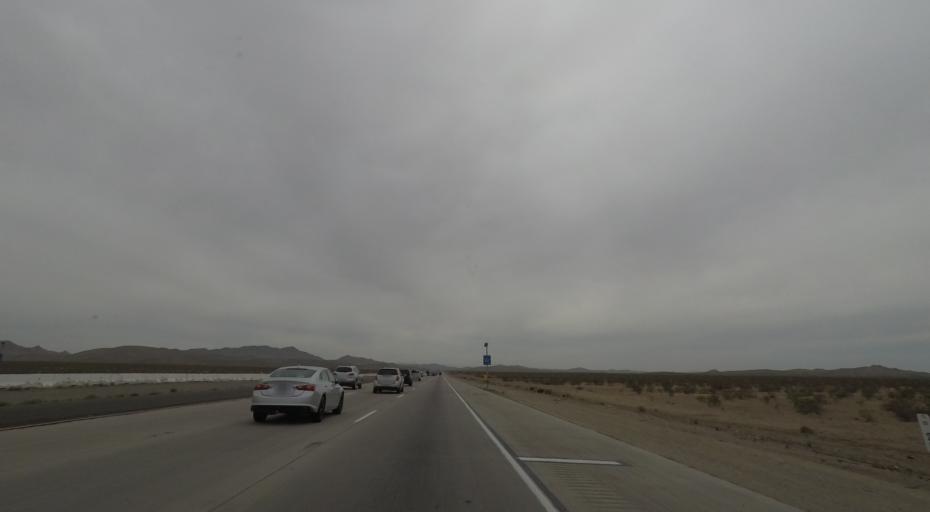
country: US
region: California
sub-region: San Bernardino County
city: Lenwood
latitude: 34.7925
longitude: -117.1182
